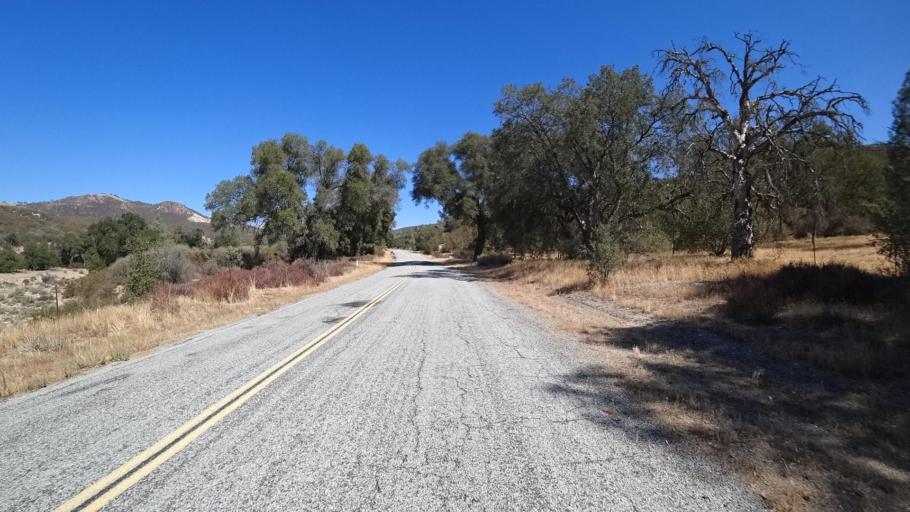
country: US
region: California
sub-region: San Luis Obispo County
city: San Miguel
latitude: 35.8938
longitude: -120.5554
